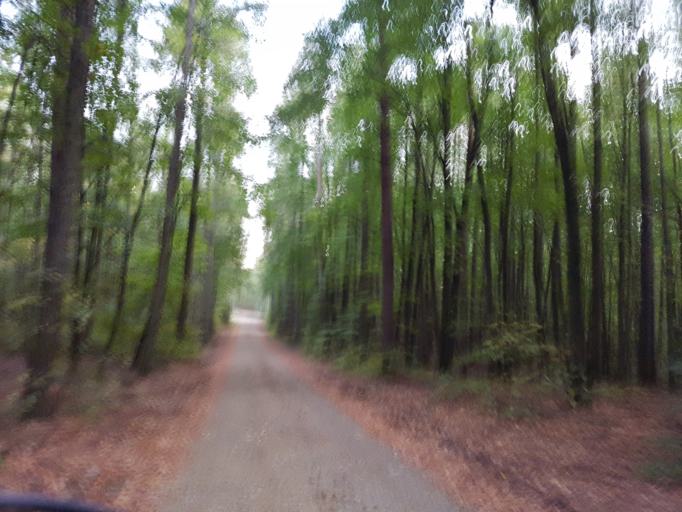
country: DE
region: Brandenburg
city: Trobitz
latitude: 51.5666
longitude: 13.4461
